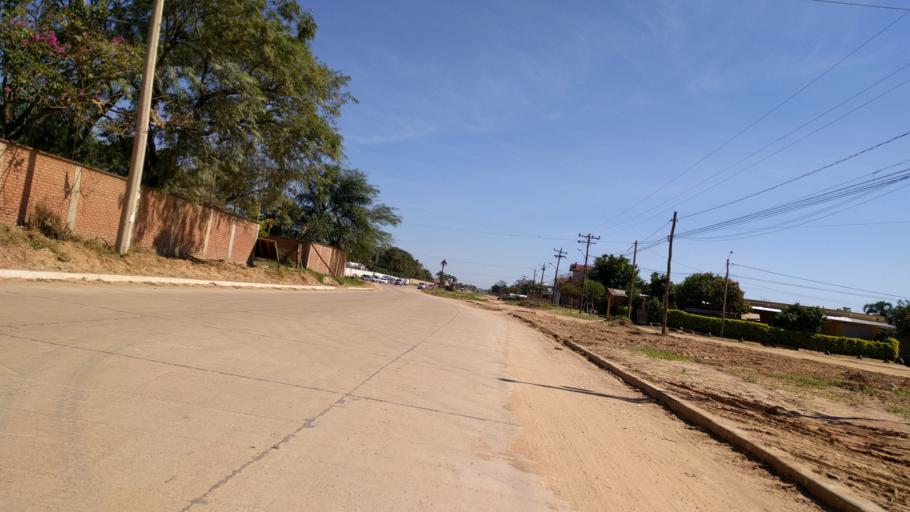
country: BO
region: Santa Cruz
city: Santa Cruz de la Sierra
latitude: -17.8444
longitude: -63.2292
